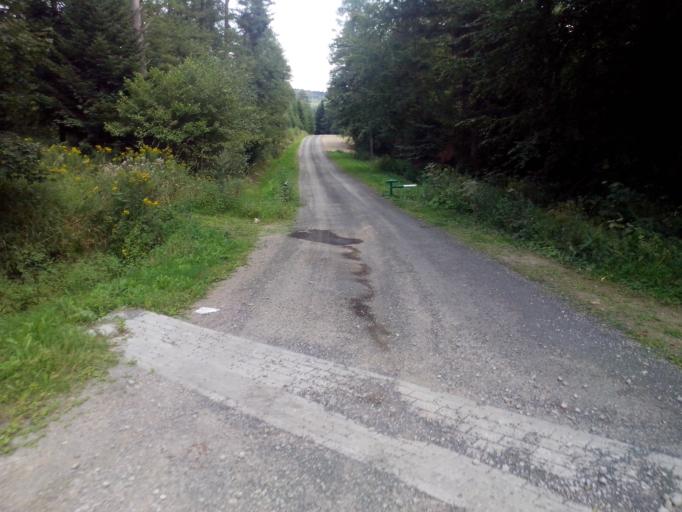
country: PL
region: Subcarpathian Voivodeship
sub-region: Powiat strzyzowski
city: Wysoka Strzyzowska
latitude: 49.8128
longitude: 21.7885
